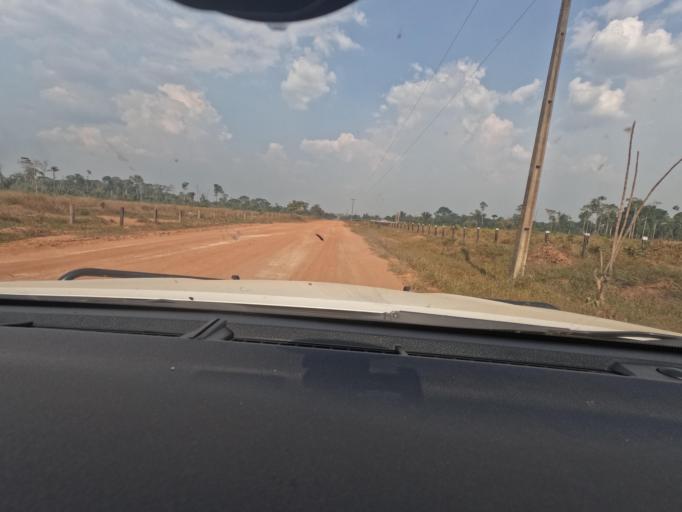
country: BR
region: Rondonia
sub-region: Porto Velho
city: Porto Velho
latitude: -8.6830
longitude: -63.1987
